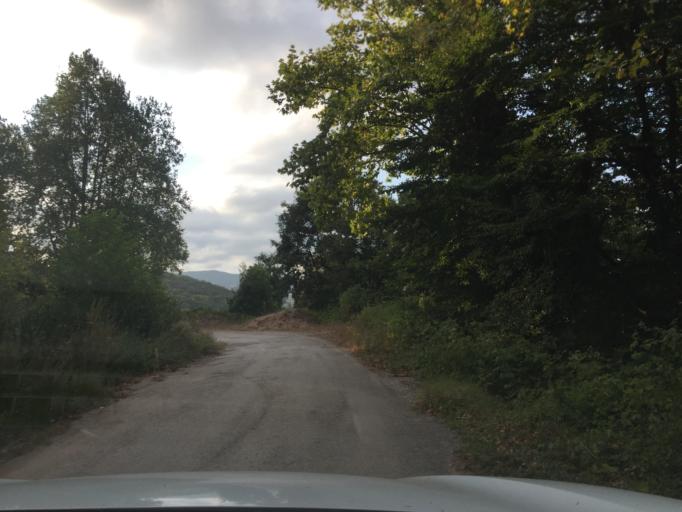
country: TR
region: Balikesir
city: Gonen
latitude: 40.0297
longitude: 27.5644
